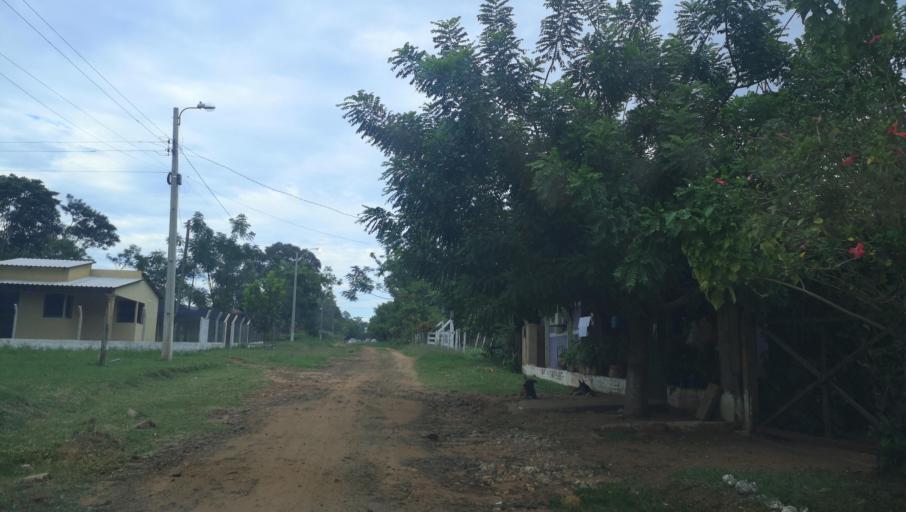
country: PY
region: San Pedro
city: Capiibary
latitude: -24.7421
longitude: -56.0266
